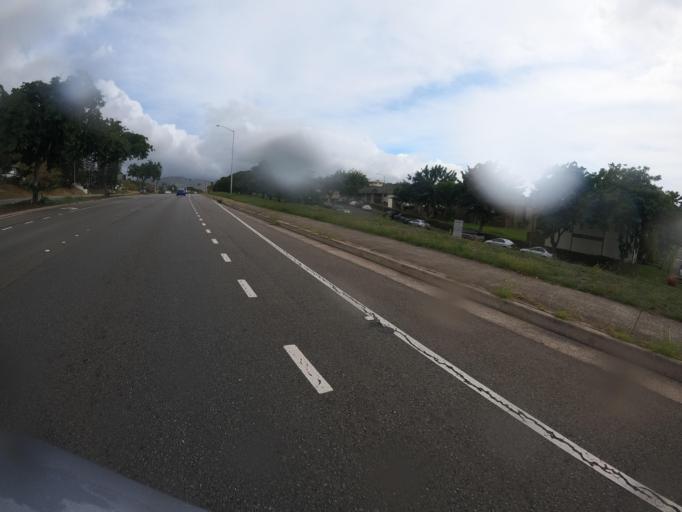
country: US
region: Hawaii
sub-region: Honolulu County
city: Halawa
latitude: 21.3669
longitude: -157.9264
